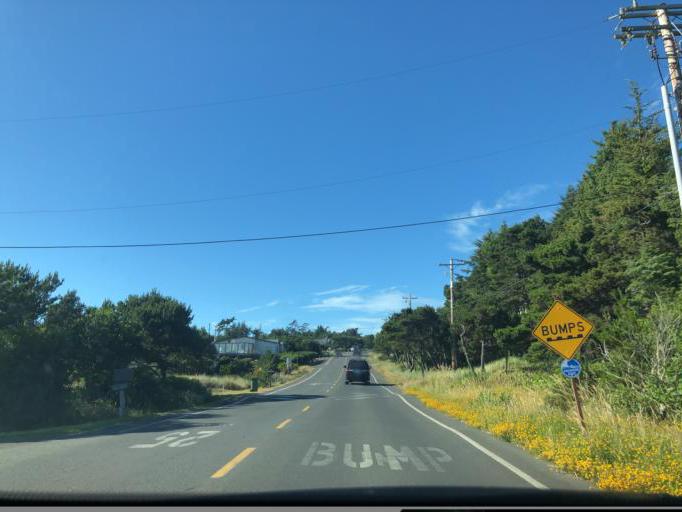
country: US
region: Oregon
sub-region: Lincoln County
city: Waldport
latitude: 44.4376
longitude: -124.0788
